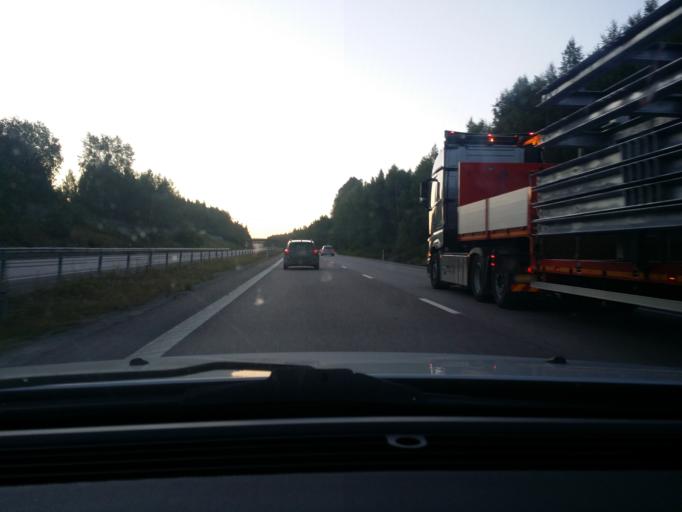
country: SE
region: Uppsala
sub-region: Enkopings Kommun
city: Enkoping
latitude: 59.6520
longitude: 17.1057
